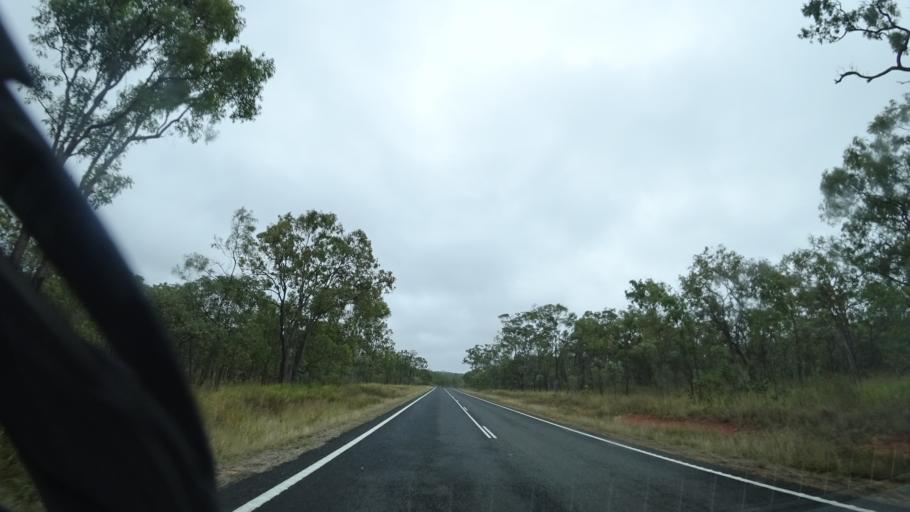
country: AU
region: Queensland
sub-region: Tablelands
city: Ravenshoe
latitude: -17.6851
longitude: 145.1395
